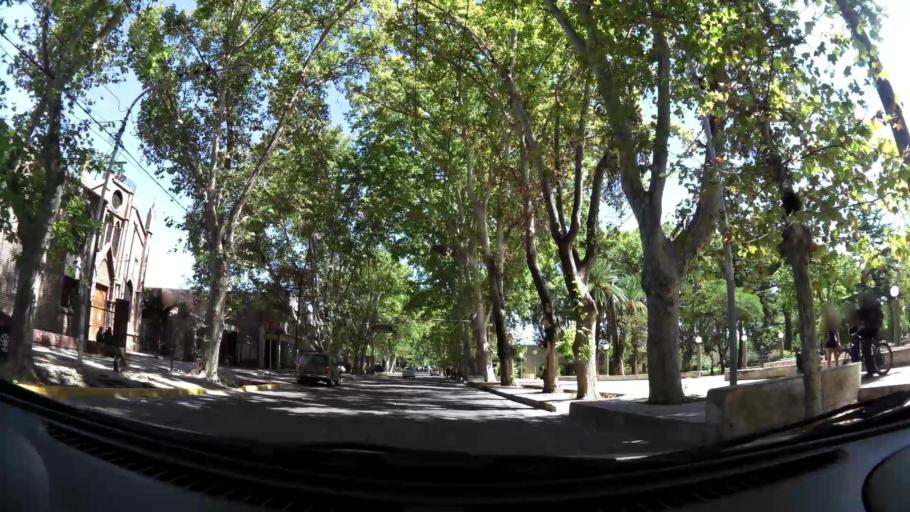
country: AR
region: Mendoza
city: Mendoza
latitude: -32.8942
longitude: -68.8243
